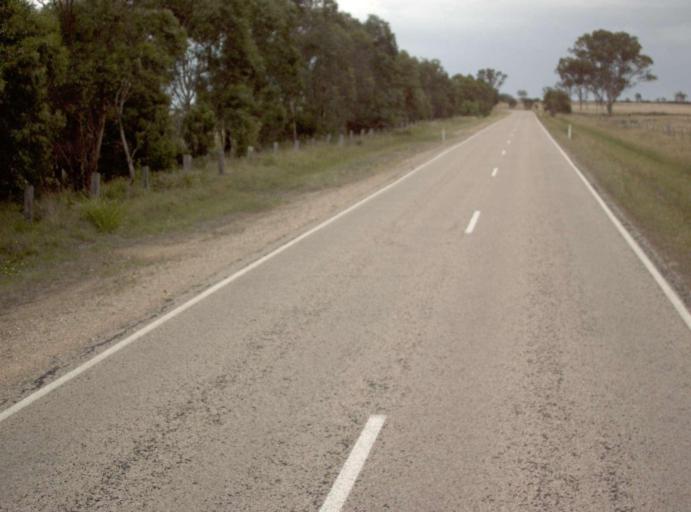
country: AU
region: Victoria
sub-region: East Gippsland
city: Bairnsdale
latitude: -37.9002
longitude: 147.5532
